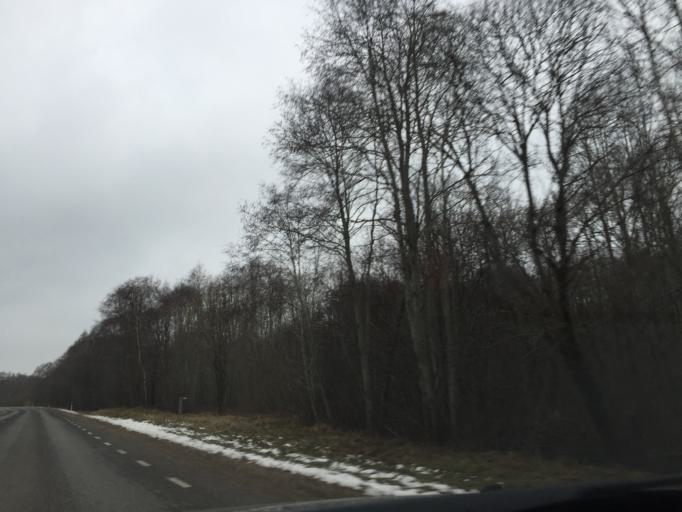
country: EE
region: Saare
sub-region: Kuressaare linn
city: Kuressaare
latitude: 58.2941
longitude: 22.3729
